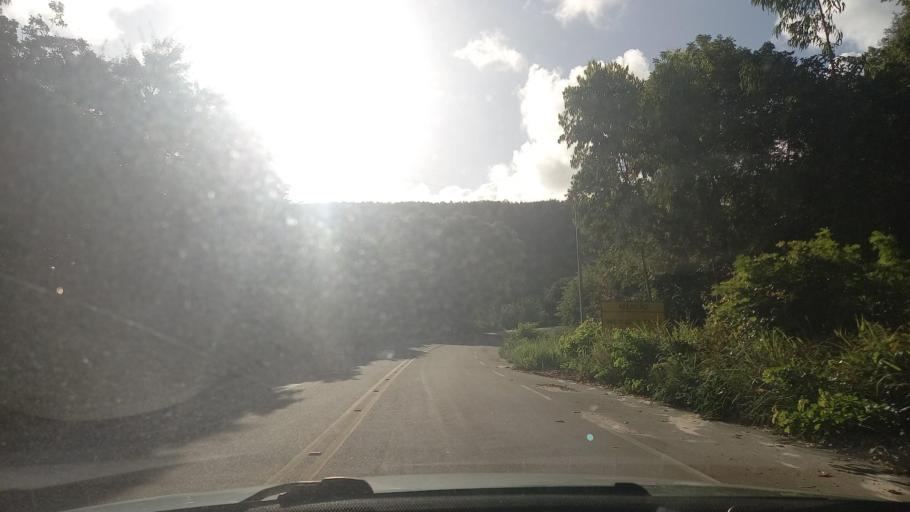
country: BR
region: Alagoas
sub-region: Marechal Deodoro
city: Marechal Deodoro
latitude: -9.8367
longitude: -35.9282
